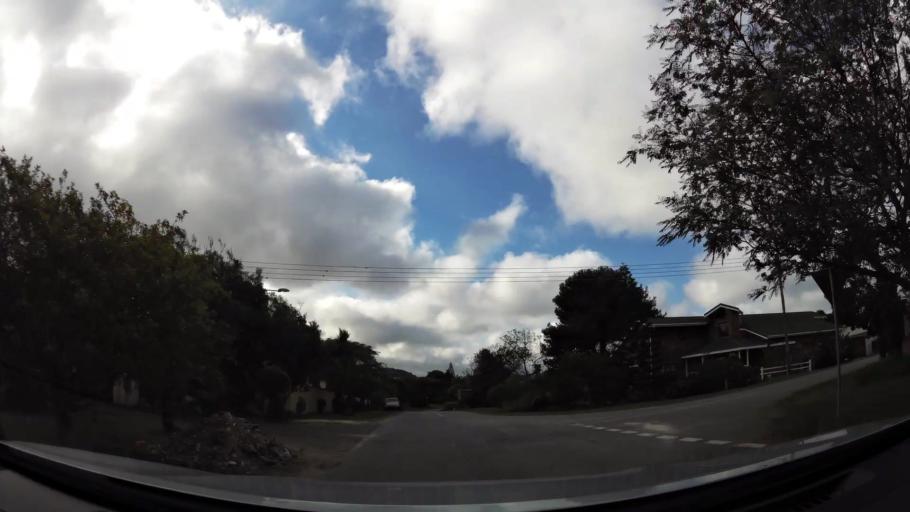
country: ZA
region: Western Cape
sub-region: Eden District Municipality
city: Plettenberg Bay
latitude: -34.0730
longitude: 23.3684
